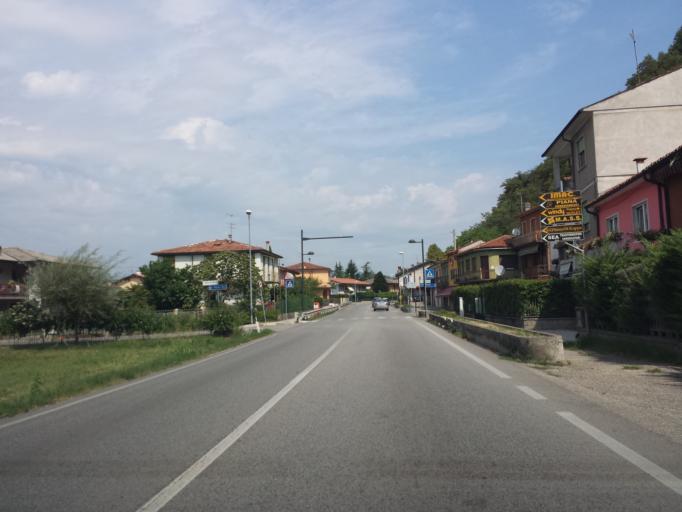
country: IT
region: Veneto
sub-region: Provincia di Vicenza
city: Tezze
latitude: 45.5376
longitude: 11.3851
